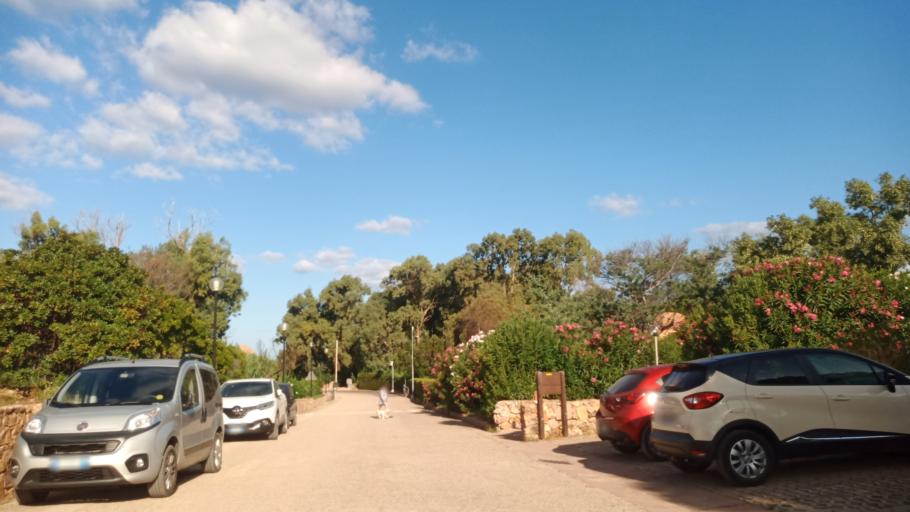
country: IT
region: Sardinia
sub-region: Provincia di Olbia-Tempio
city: Trinita d'Agultu
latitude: 41.0233
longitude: 8.8958
